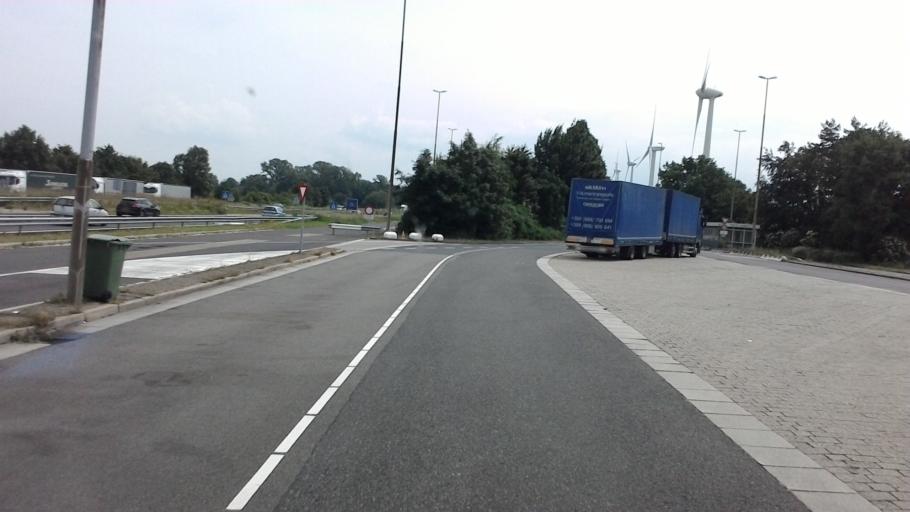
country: NL
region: Limburg
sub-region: Gemeente Simpelveld
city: Simpelveld
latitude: 50.8193
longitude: 6.0236
